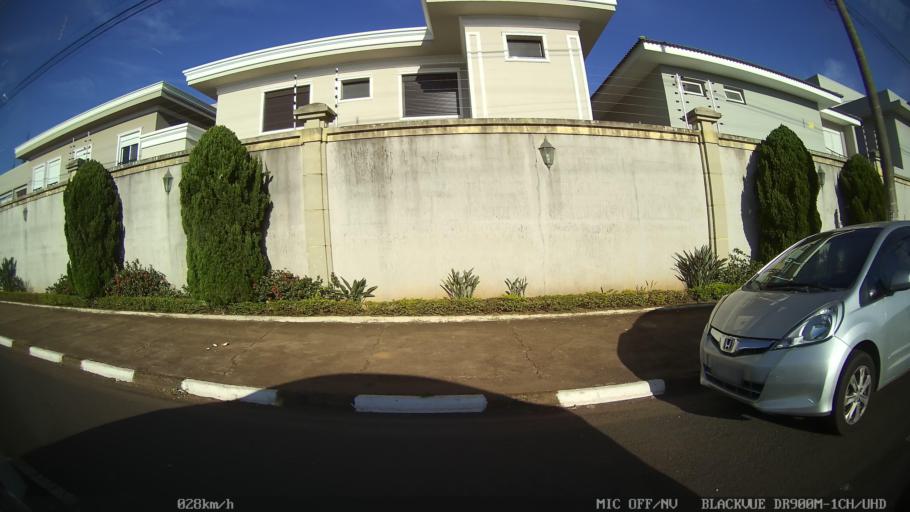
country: BR
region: Sao Paulo
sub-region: Franca
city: Franca
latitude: -20.5139
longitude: -47.3775
